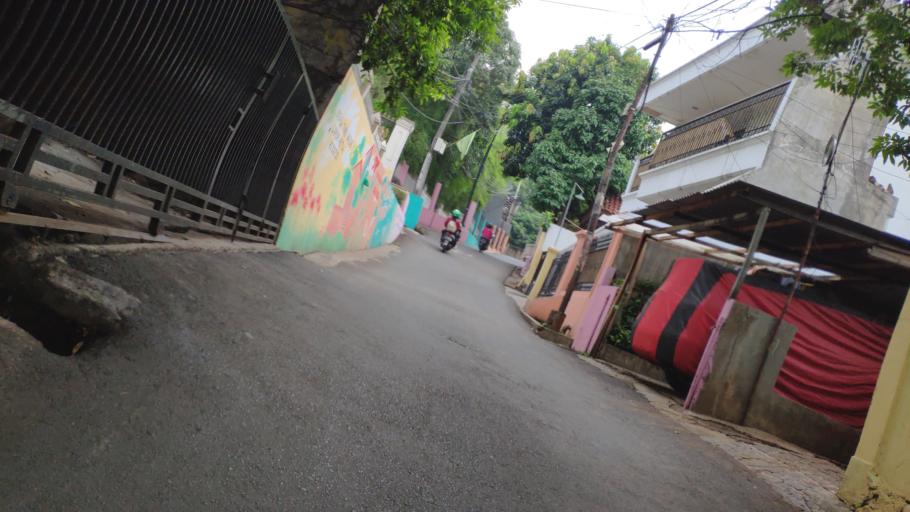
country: ID
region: Jakarta Raya
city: Jakarta
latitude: -6.3053
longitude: 106.8326
